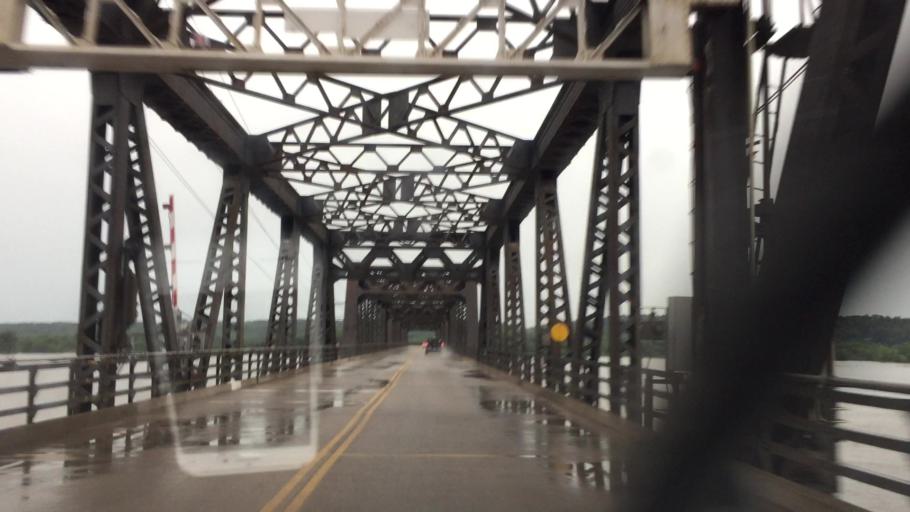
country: US
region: Iowa
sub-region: Lee County
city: Fort Madison
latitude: 40.6265
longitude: -91.2954
